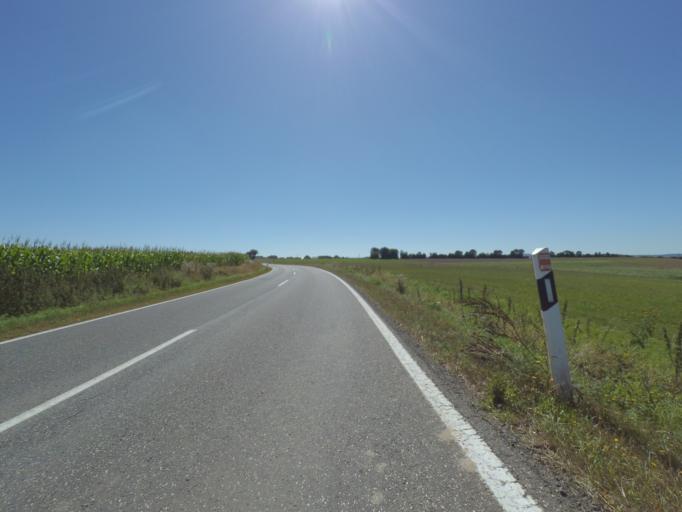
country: DE
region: Rheinland-Pfalz
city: Beuren
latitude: 50.1006
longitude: 7.0717
